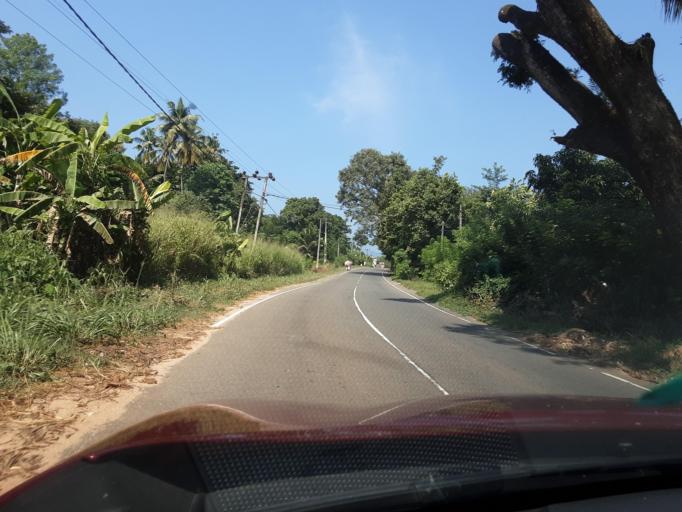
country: LK
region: Uva
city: Badulla
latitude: 7.1839
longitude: 81.0440
